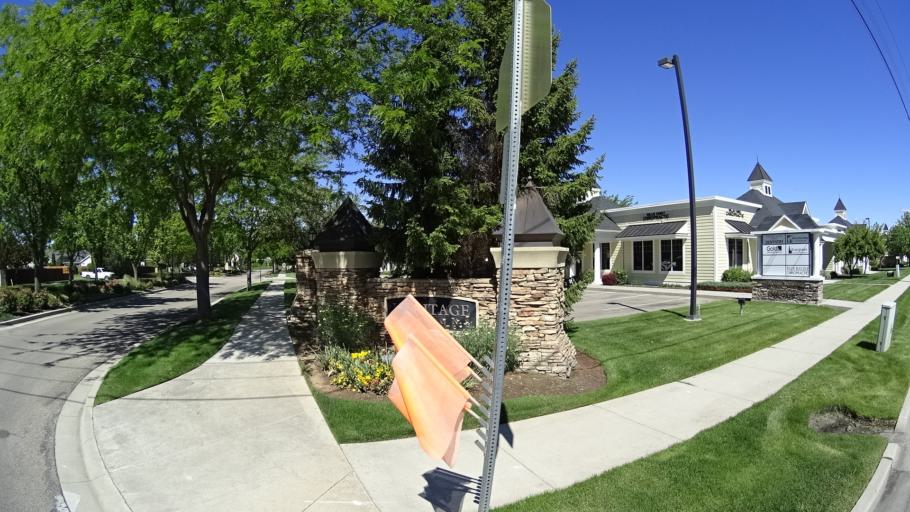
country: US
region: Idaho
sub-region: Ada County
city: Meridian
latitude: 43.6396
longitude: -116.3746
